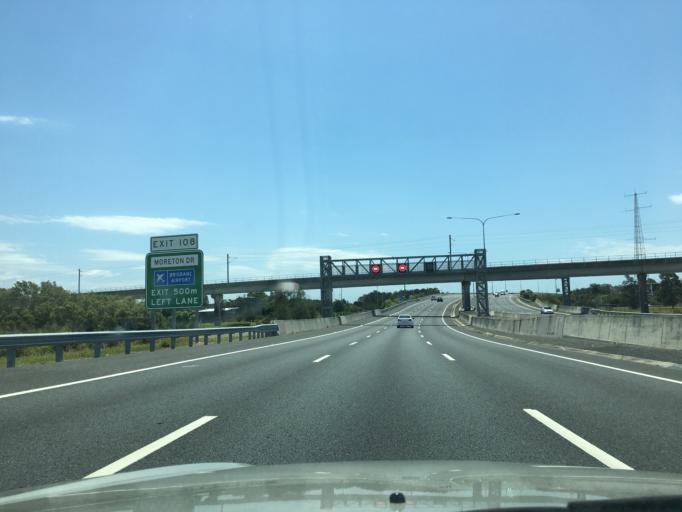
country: AU
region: Queensland
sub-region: Brisbane
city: Ascot
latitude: -27.4165
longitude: 153.0869
